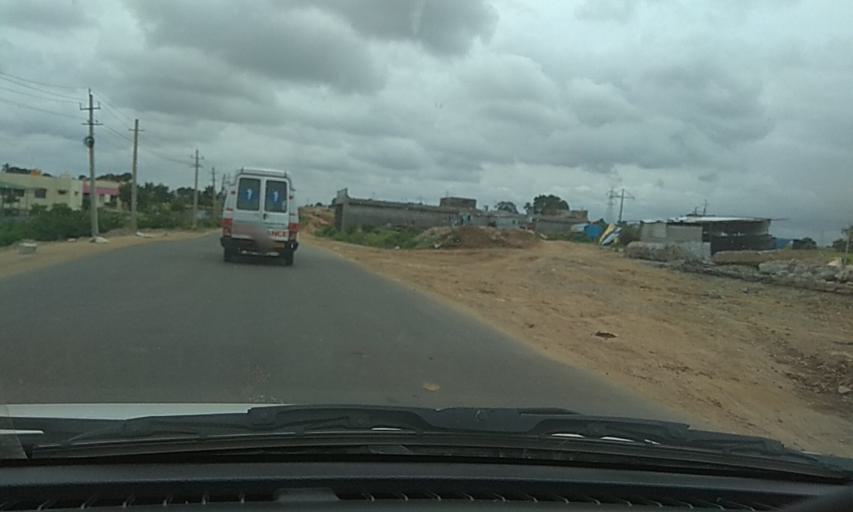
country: IN
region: Karnataka
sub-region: Chitradurga
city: Chitradurga
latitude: 14.2901
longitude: 76.2881
